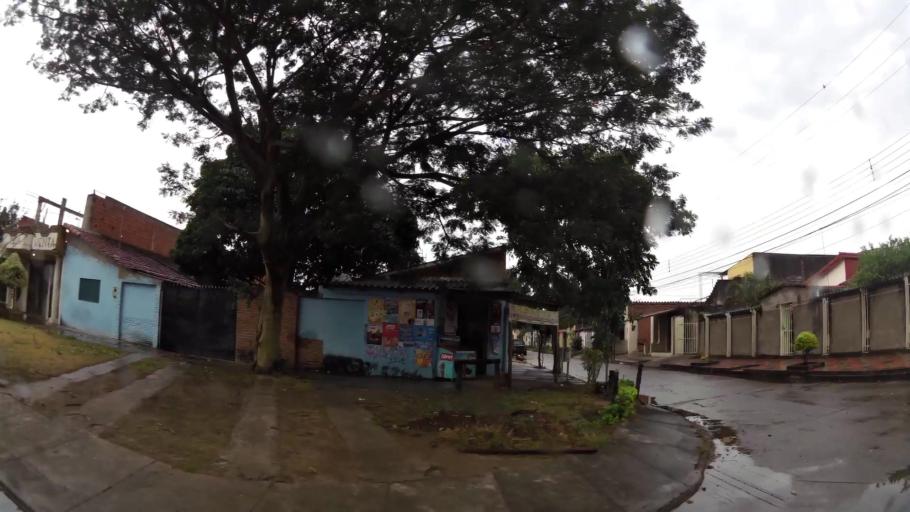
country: BO
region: Santa Cruz
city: Santa Cruz de la Sierra
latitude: -17.7629
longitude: -63.1529
